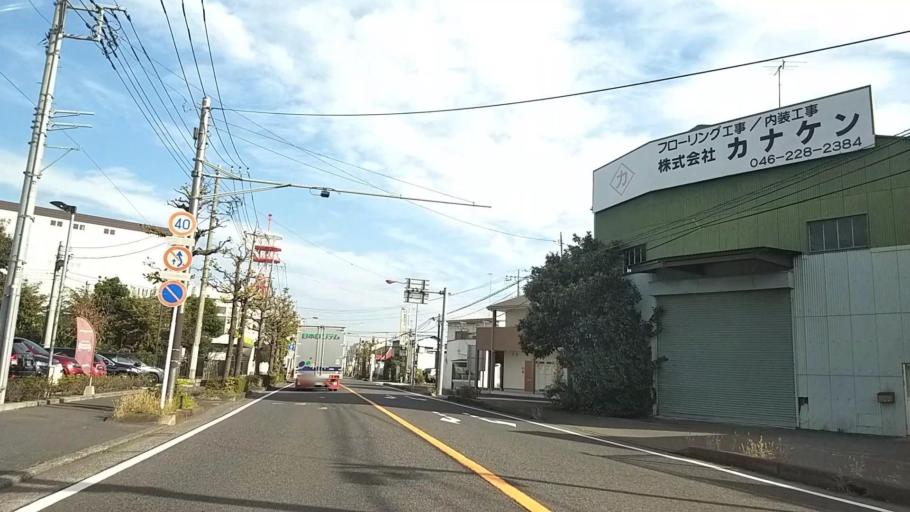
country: JP
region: Kanagawa
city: Atsugi
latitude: 35.4150
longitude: 139.3634
